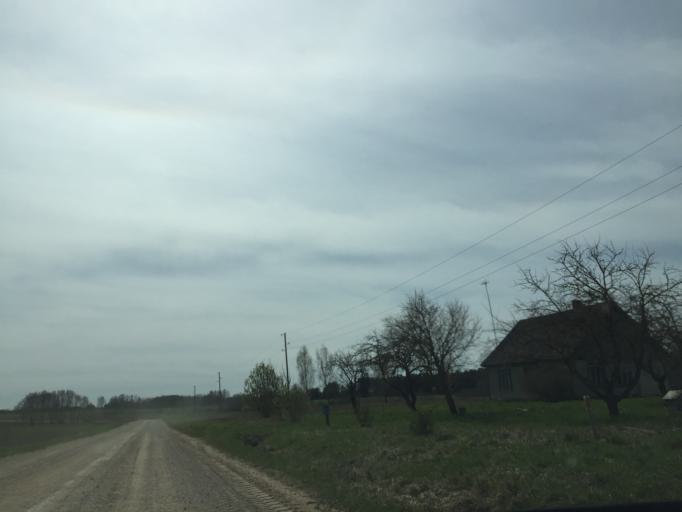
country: LV
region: Ludzas Rajons
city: Ludza
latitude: 56.5733
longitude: 27.5502
